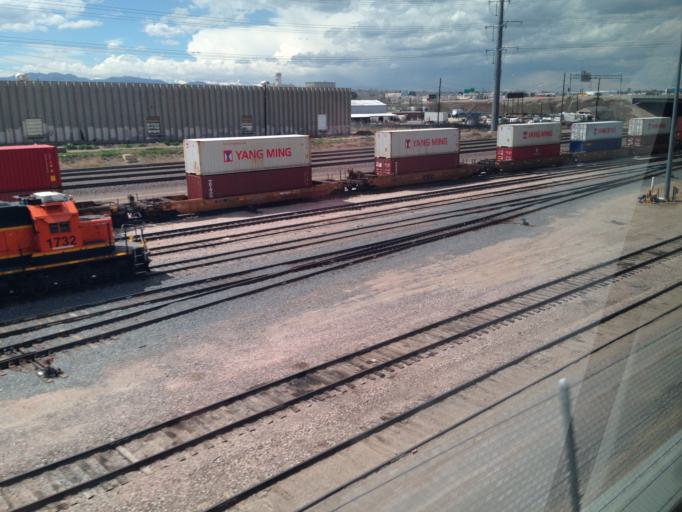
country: US
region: Colorado
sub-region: Adams County
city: Berkley
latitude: 39.7808
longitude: -104.9971
